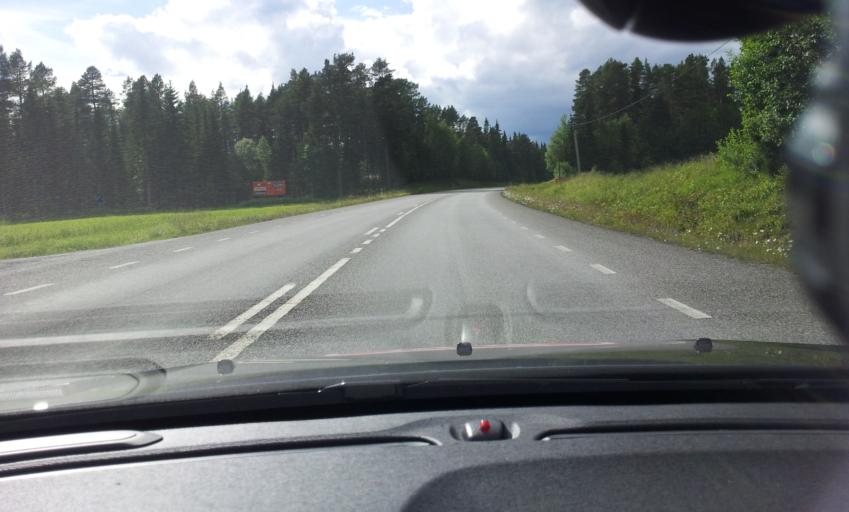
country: SE
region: Jaemtland
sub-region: Are Kommun
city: Jarpen
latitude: 63.3364
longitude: 13.5080
